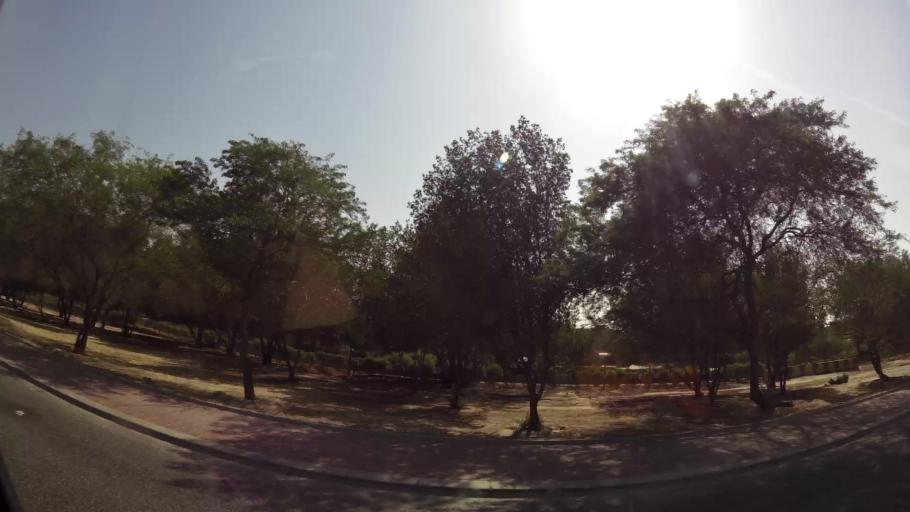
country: KW
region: Mubarak al Kabir
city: Sabah as Salim
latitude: 29.2644
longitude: 48.0507
